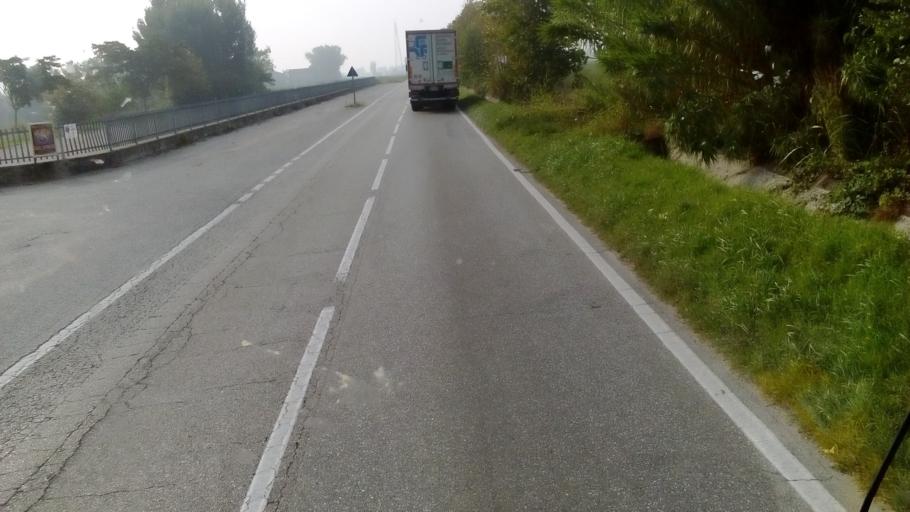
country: IT
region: Veneto
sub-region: Provincia di Verona
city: Buttapietra
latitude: 45.3449
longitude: 10.9738
